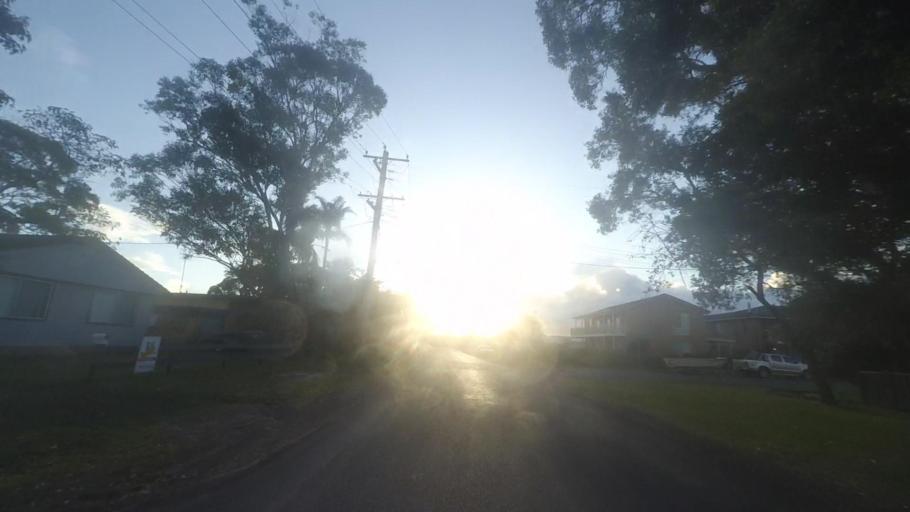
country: AU
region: New South Wales
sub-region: Great Lakes
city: Hawks Nest
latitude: -32.6696
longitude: 152.1720
